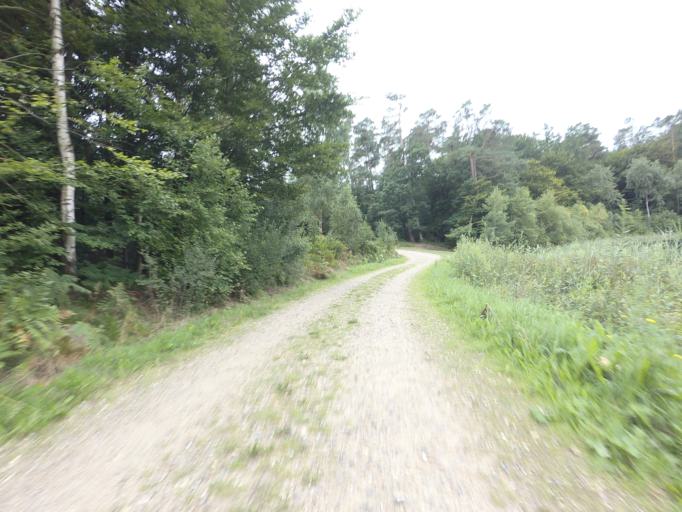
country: DK
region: Central Jutland
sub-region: Silkeborg Kommune
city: Virklund
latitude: 56.0343
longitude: 9.4728
